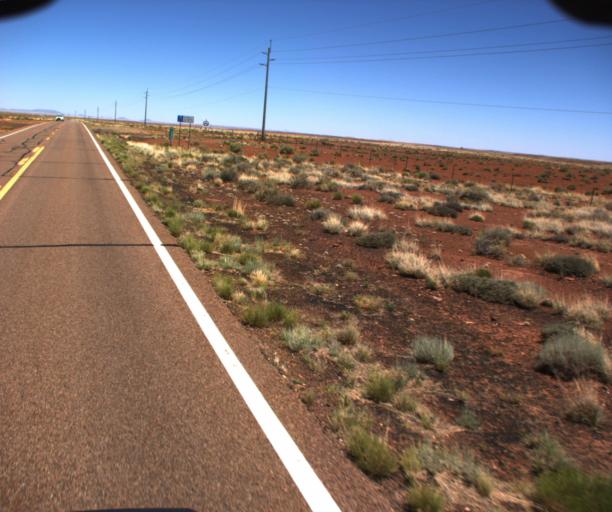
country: US
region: Arizona
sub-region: Coconino County
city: LeChee
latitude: 34.9288
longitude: -110.8017
